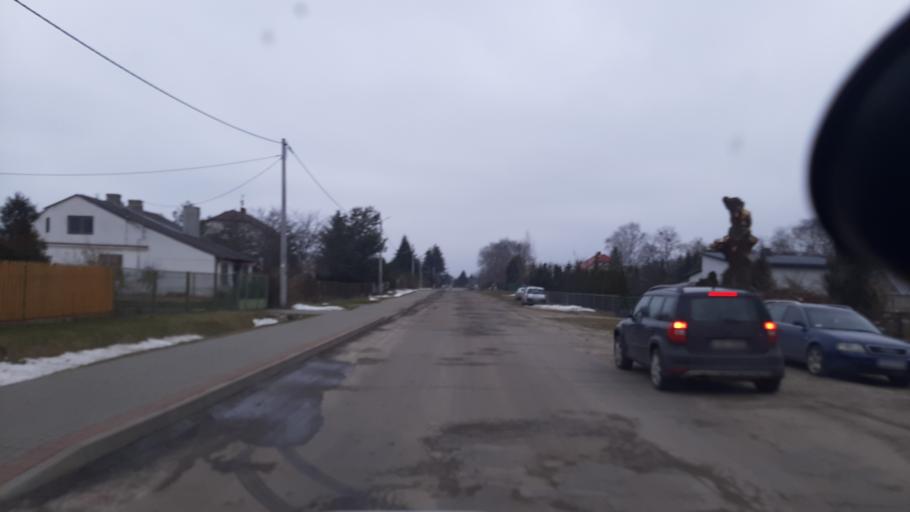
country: PL
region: Lublin Voivodeship
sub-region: Powiat wlodawski
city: Wlodawa
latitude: 51.5224
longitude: 23.5784
